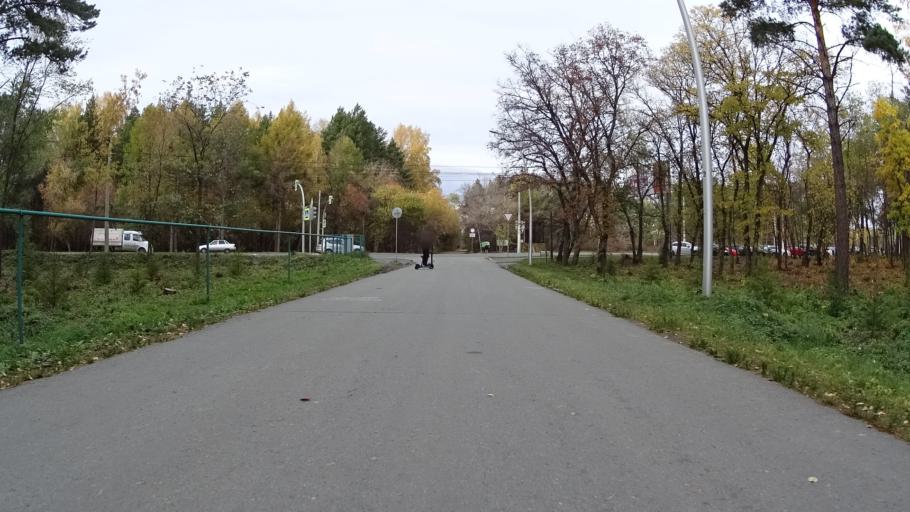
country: RU
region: Chelyabinsk
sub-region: Gorod Chelyabinsk
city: Chelyabinsk
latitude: 55.1465
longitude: 61.3536
